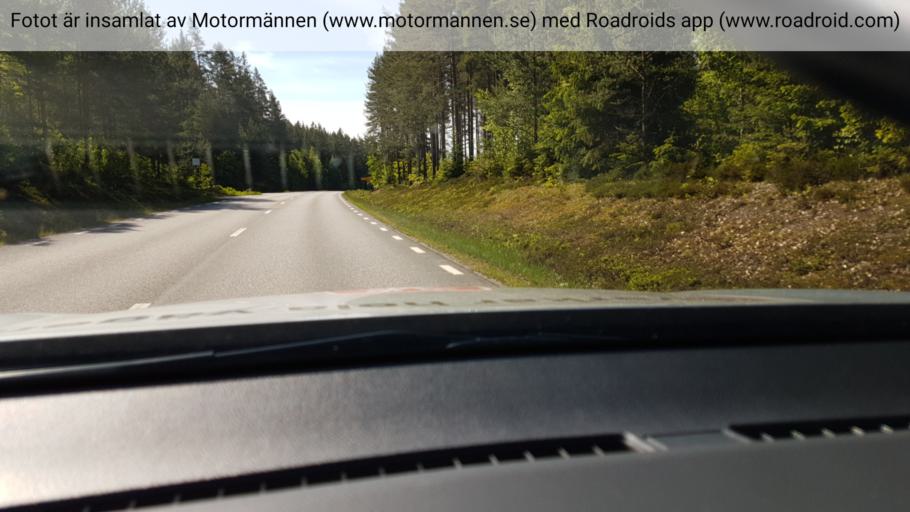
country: SE
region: Vaestra Goetaland
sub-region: Tibro Kommun
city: Tibro
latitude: 58.3931
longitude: 14.2008
